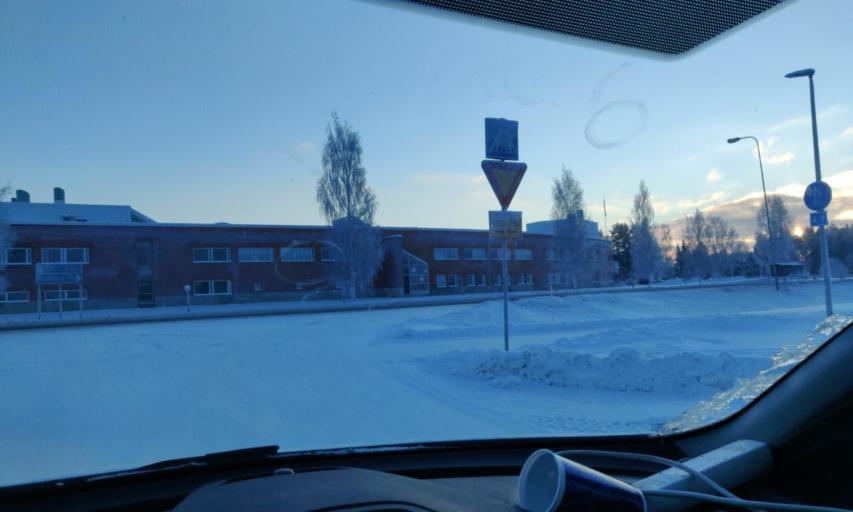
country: FI
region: Northern Ostrobothnia
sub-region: Ylivieska
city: Ylivieska
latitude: 64.0745
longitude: 24.5130
